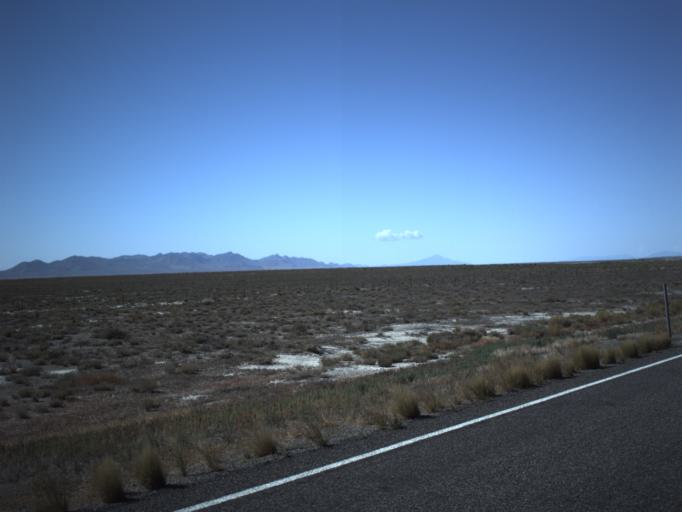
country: US
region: Utah
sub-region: Millard County
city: Delta
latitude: 39.2392
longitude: -112.9166
